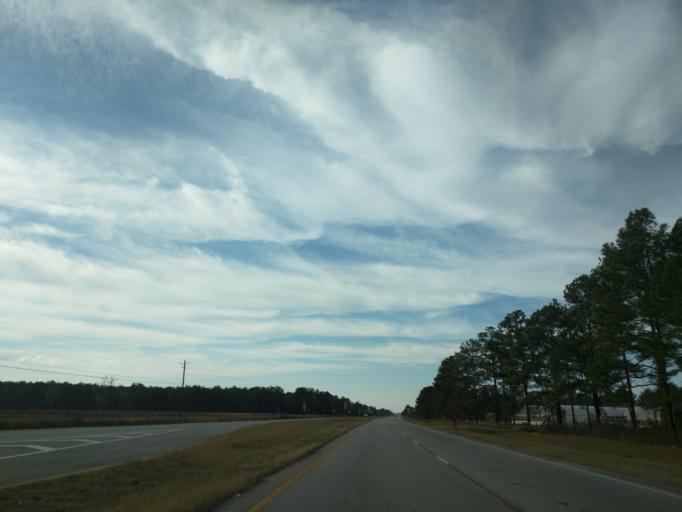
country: US
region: Georgia
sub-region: Decatur County
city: Bainbridge
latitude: 30.8891
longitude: -84.4832
